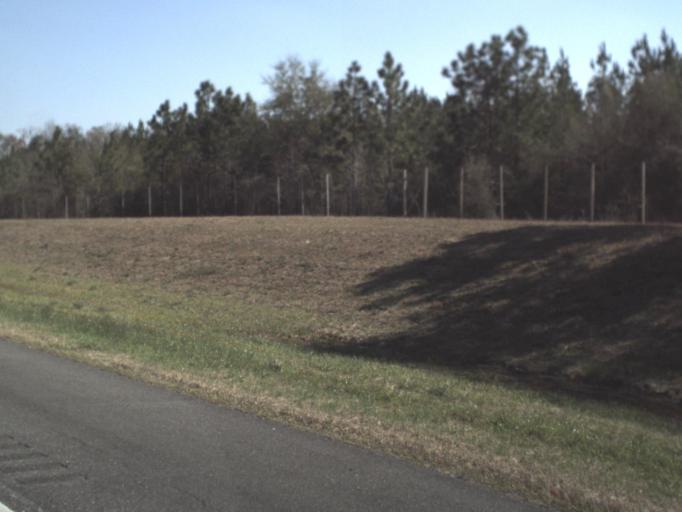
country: US
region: Florida
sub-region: Jackson County
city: Marianna
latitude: 30.7177
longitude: -85.1686
